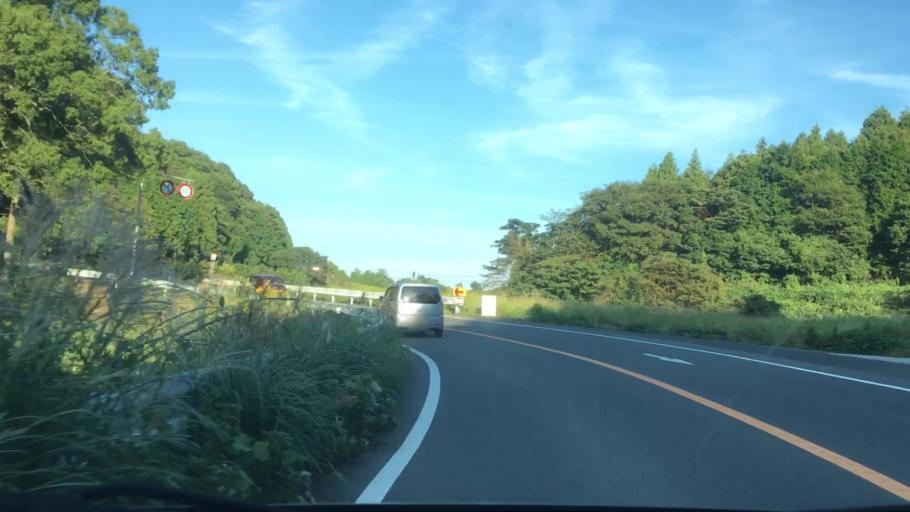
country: JP
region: Nagasaki
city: Sasebo
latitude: 33.0407
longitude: 129.6918
